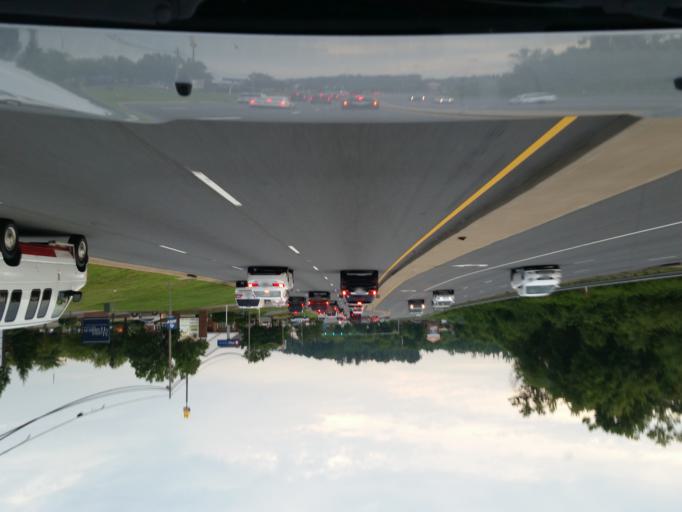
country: US
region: Virginia
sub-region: City of Fredericksburg
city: Fredericksburg
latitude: 38.2301
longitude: -77.5046
